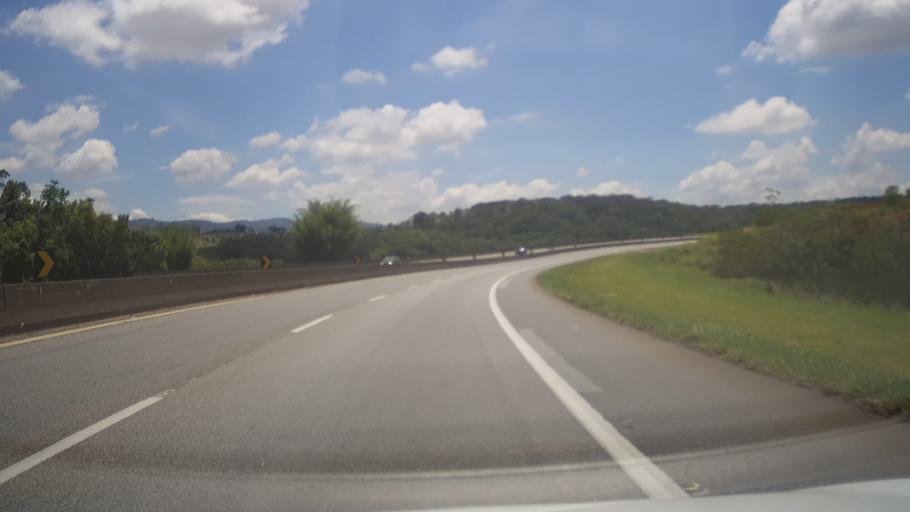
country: BR
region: Minas Gerais
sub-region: Sao Goncalo Do Sapucai
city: Sao Goncalo do Sapucai
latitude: -21.9228
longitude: -45.6117
